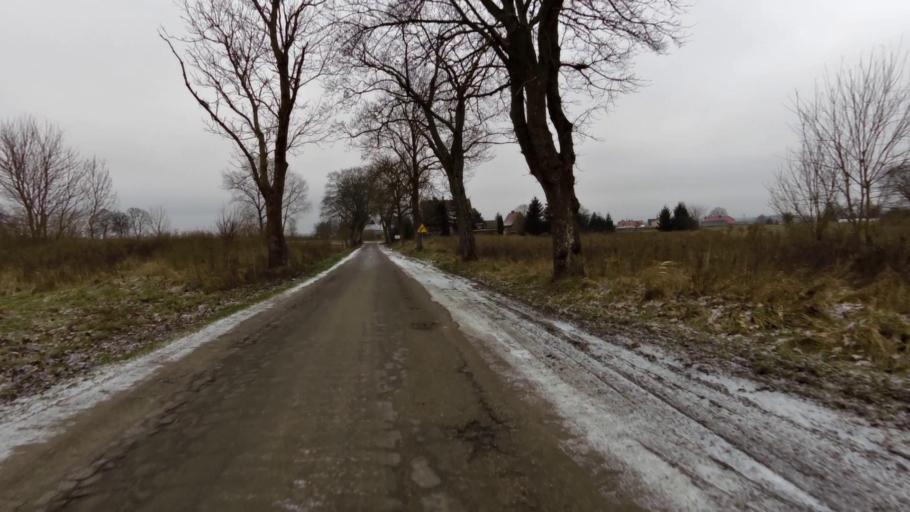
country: PL
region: West Pomeranian Voivodeship
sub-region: Powiat szczecinecki
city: Szczecinek
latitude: 53.6537
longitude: 16.6340
